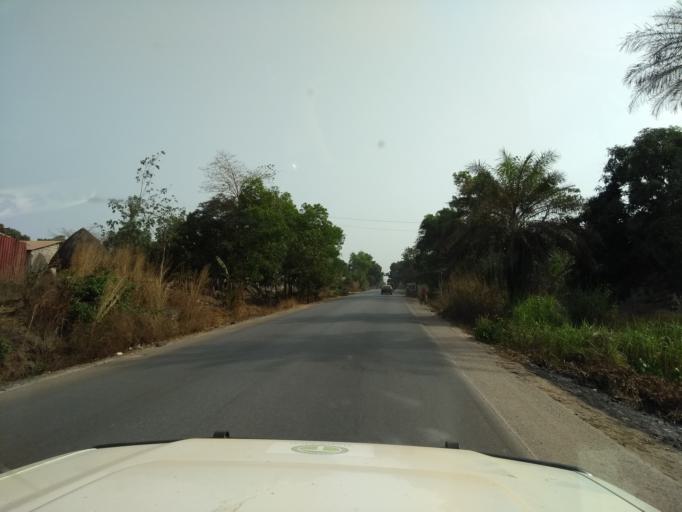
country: GN
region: Kindia
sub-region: Prefecture de Dubreka
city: Dubreka
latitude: 9.8467
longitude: -13.4862
